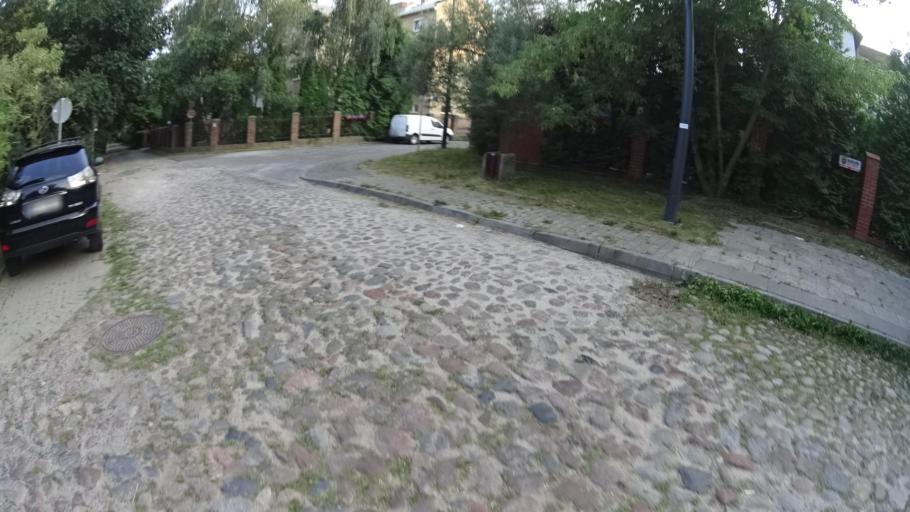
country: PL
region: Masovian Voivodeship
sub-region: Warszawa
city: Ursynow
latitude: 52.1464
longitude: 21.0658
